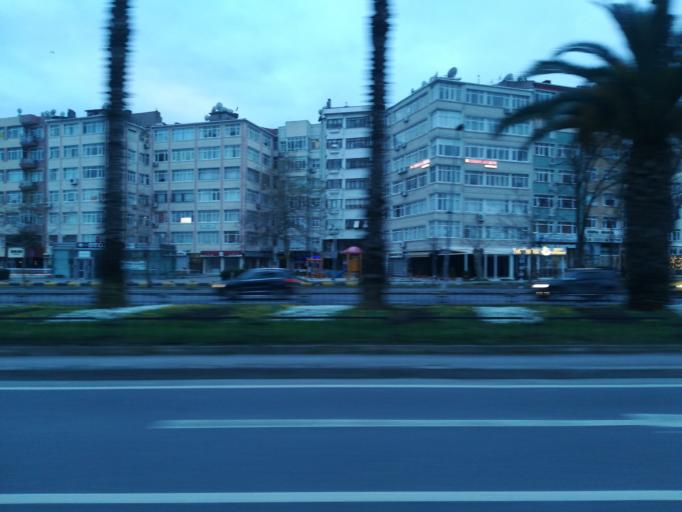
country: TR
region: Istanbul
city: Istanbul
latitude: 41.0134
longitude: 28.9456
